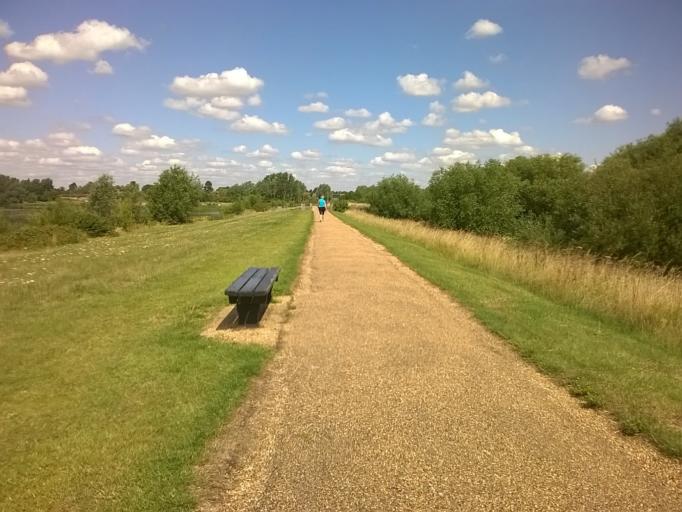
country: GB
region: England
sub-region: Milton Keynes
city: Broughton
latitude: 52.0568
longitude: -0.7144
